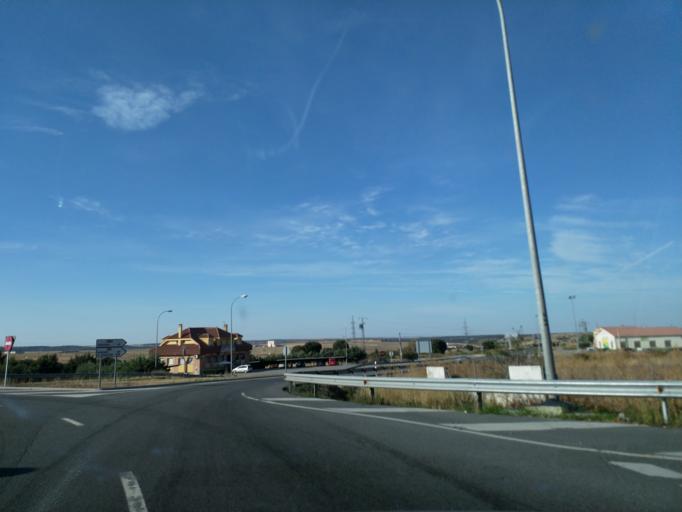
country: ES
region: Castille and Leon
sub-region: Provincia de Segovia
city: Villacastin
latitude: 40.7771
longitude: -4.4229
